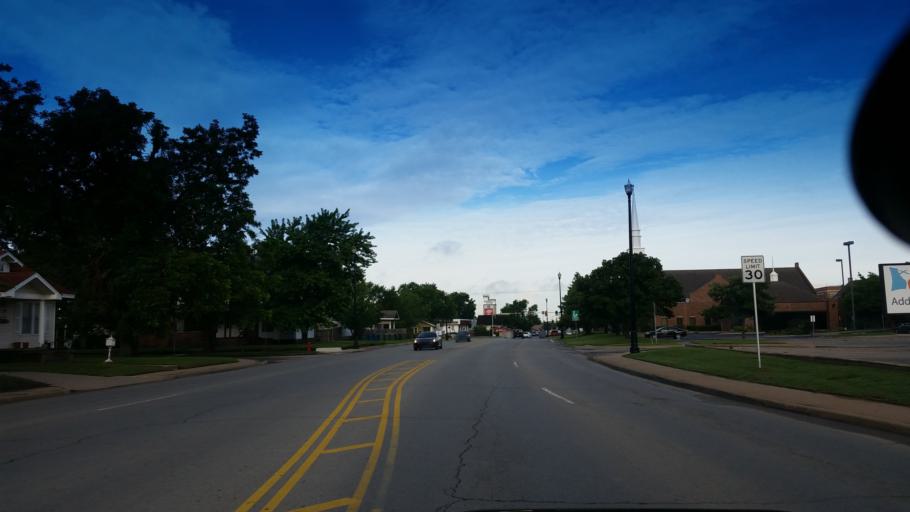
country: US
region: Oklahoma
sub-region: Oklahoma County
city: Edmond
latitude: 35.6528
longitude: -97.4760
